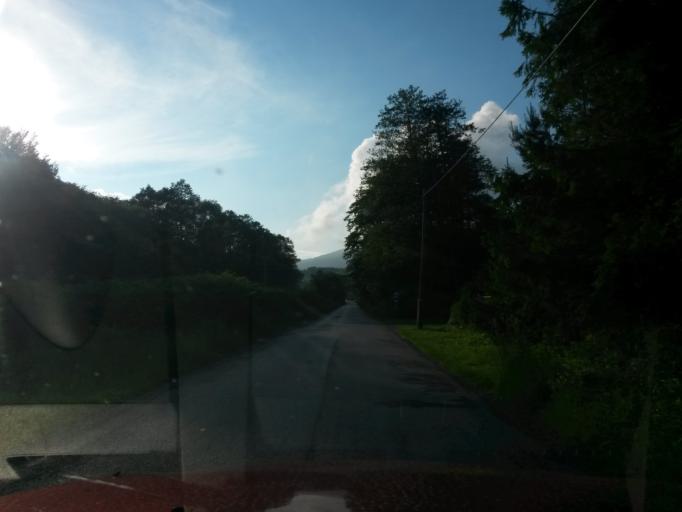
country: SK
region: Kosicky
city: Moldava nad Bodvou
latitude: 48.7369
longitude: 21.0270
